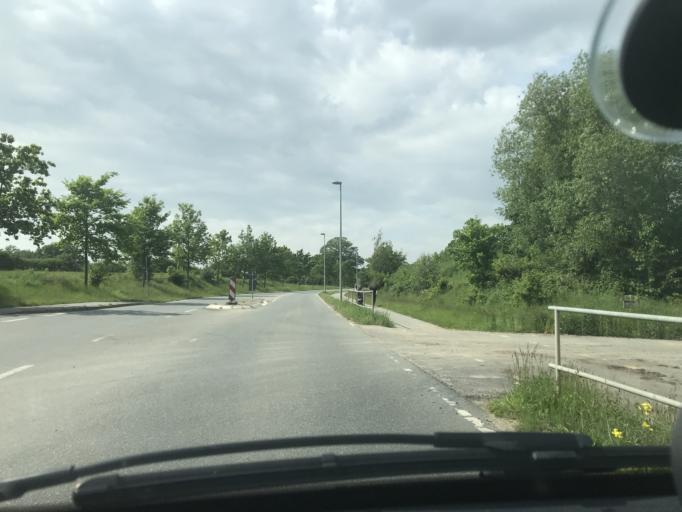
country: DE
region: Schleswig-Holstein
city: Trittau
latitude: 53.6090
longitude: 10.3960
